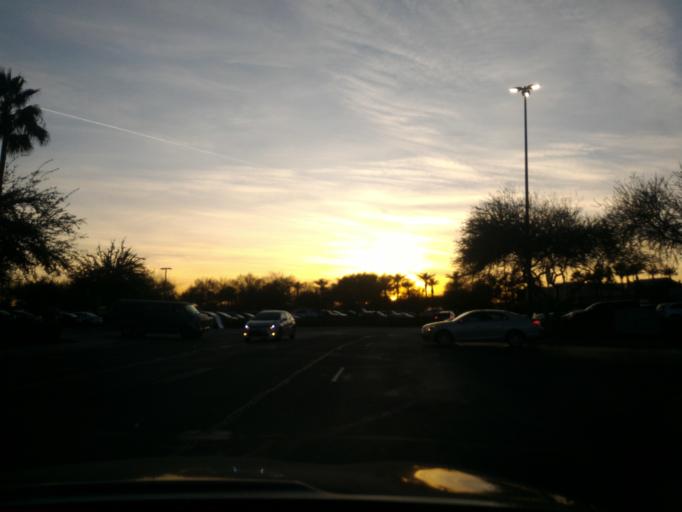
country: US
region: Arizona
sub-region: Maricopa County
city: Chandler
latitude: 33.2994
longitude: -111.8962
